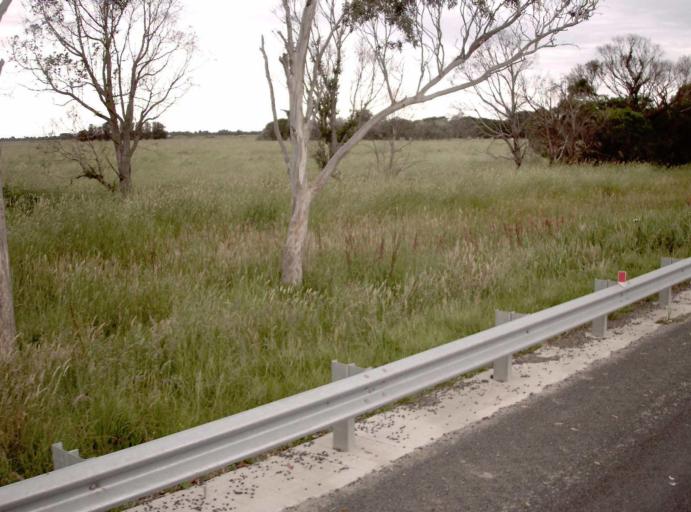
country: AU
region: Victoria
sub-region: Casey
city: Blind Bight
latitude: -38.1840
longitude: 145.3426
